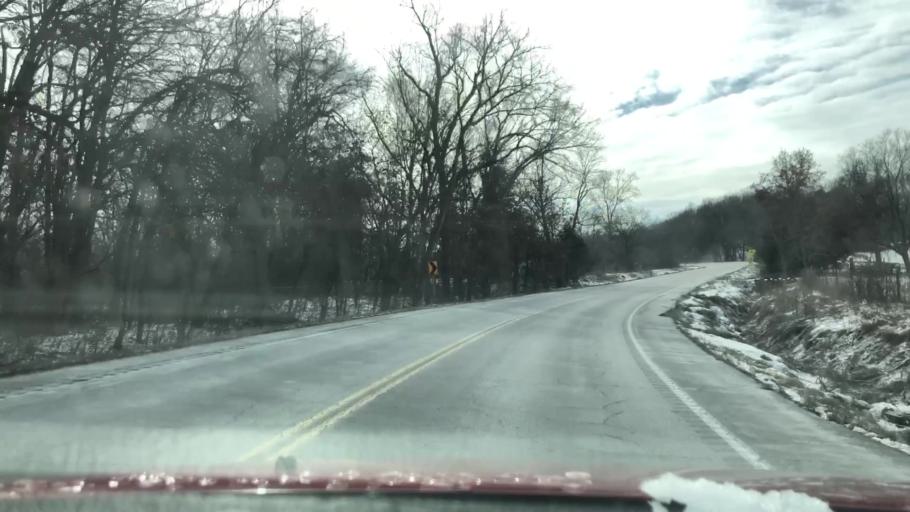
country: US
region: Missouri
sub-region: Jackson County
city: Lone Jack
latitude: 38.8981
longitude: -94.1341
